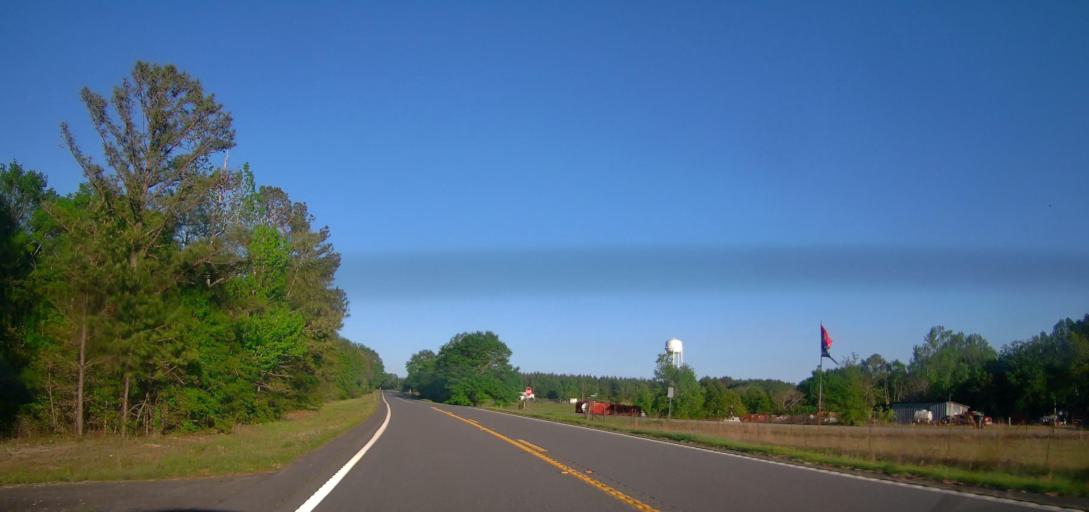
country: US
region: Georgia
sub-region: Schley County
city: Ellaville
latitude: 32.3457
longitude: -84.3707
